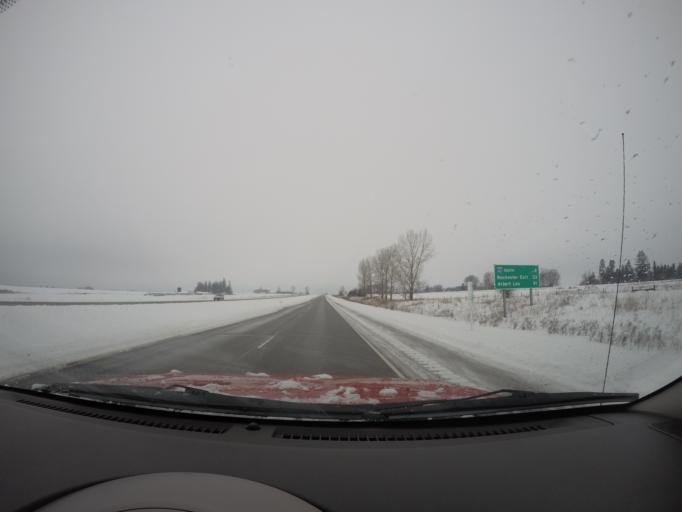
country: US
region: Minnesota
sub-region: Winona County
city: Goodview
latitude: 43.9511
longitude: -91.7019
